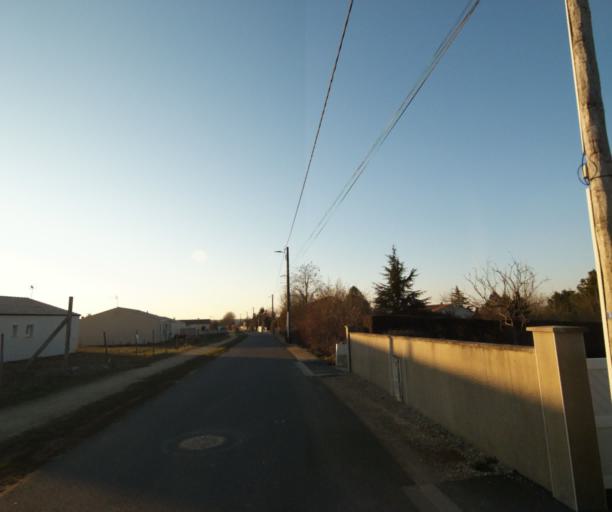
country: FR
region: Poitou-Charentes
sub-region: Departement des Deux-Sevres
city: Niort
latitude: 46.3549
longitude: -0.4457
